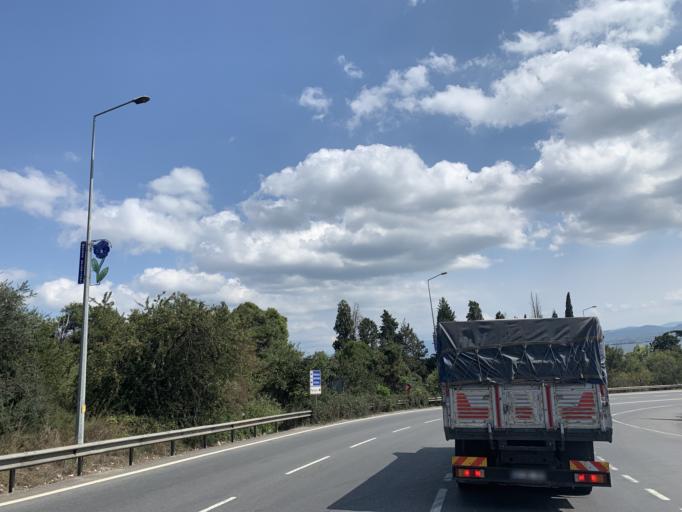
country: TR
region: Kocaeli
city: Darica
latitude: 40.7705
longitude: 29.4254
